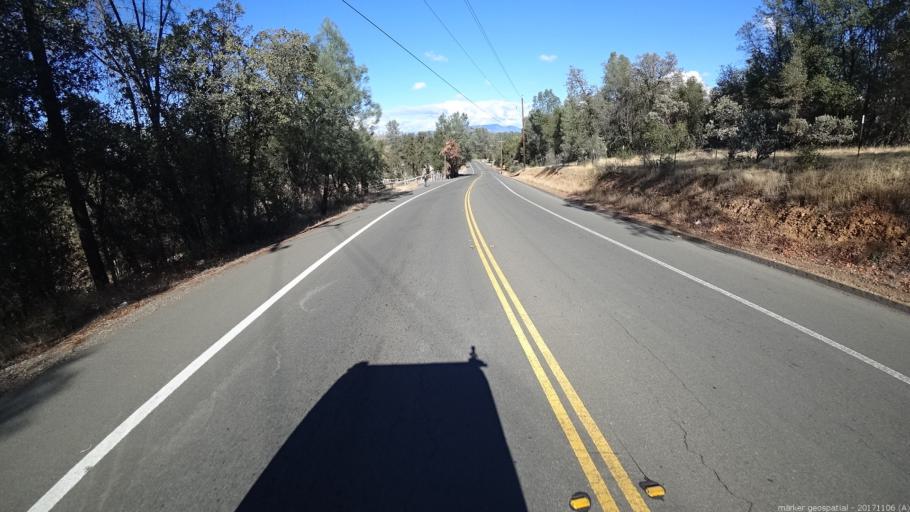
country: US
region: California
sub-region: Shasta County
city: Palo Cedro
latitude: 40.5850
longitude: -122.3070
